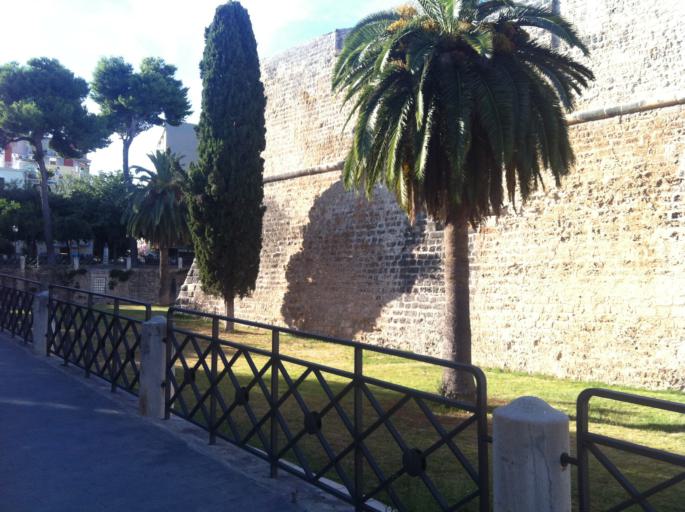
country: IT
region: Apulia
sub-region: Provincia di Foggia
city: Manfredonia
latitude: 41.6300
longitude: 15.9217
